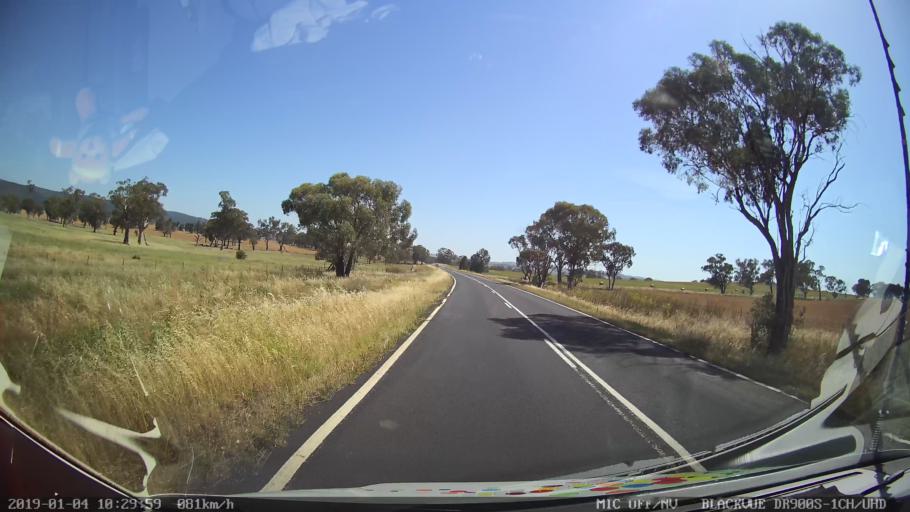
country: AU
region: New South Wales
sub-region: Cabonne
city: Canowindra
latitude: -33.3511
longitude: 148.6251
